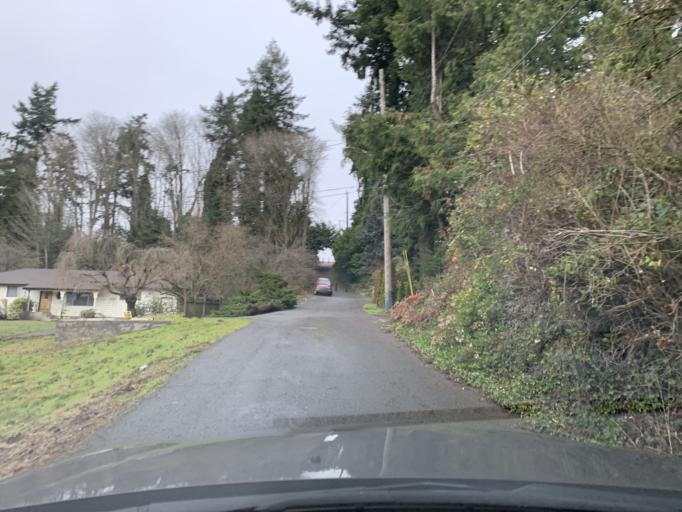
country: US
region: Washington
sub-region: King County
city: Tukwila
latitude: 47.4689
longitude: -122.2759
